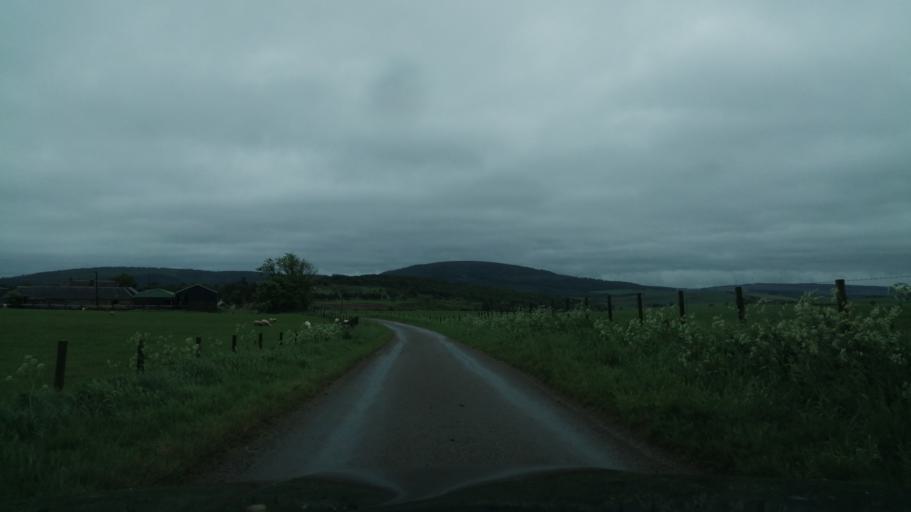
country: GB
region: Scotland
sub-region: Moray
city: Keith
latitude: 57.5737
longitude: -2.8610
